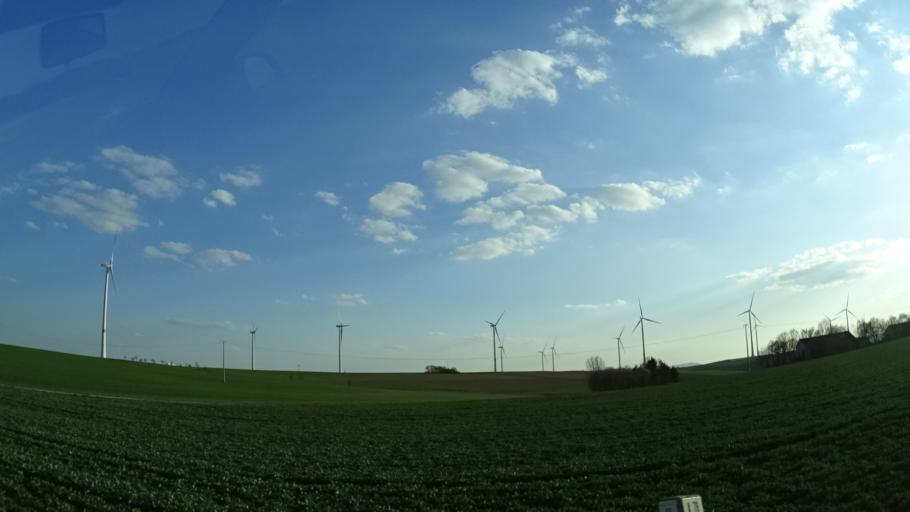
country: DE
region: Rheinland-Pfalz
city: Lettweiler
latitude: 49.7321
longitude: 7.7334
